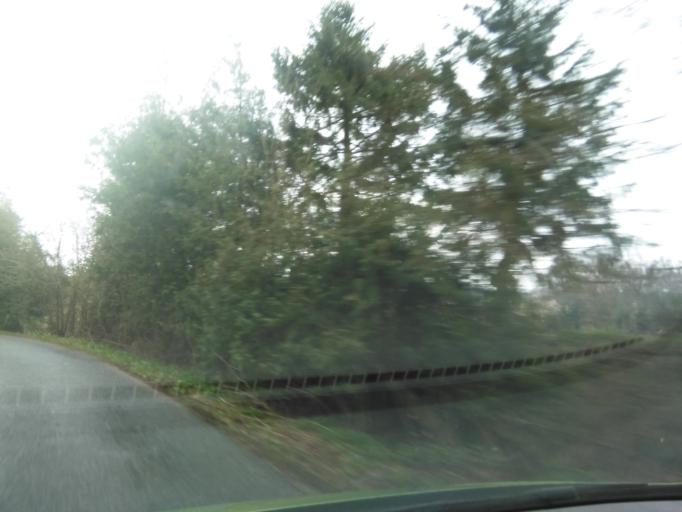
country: DK
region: Central Jutland
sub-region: Arhus Kommune
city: Stavtrup
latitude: 56.1500
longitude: 10.0821
